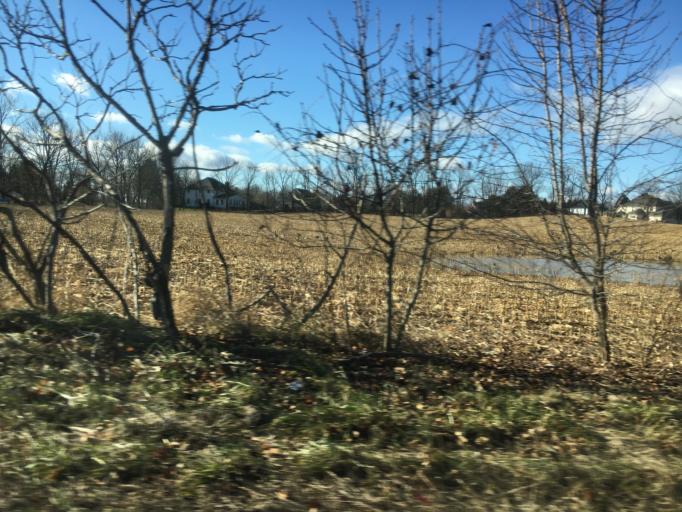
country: US
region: Pennsylvania
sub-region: Lehigh County
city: Egypt
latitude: 40.6424
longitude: -75.5459
